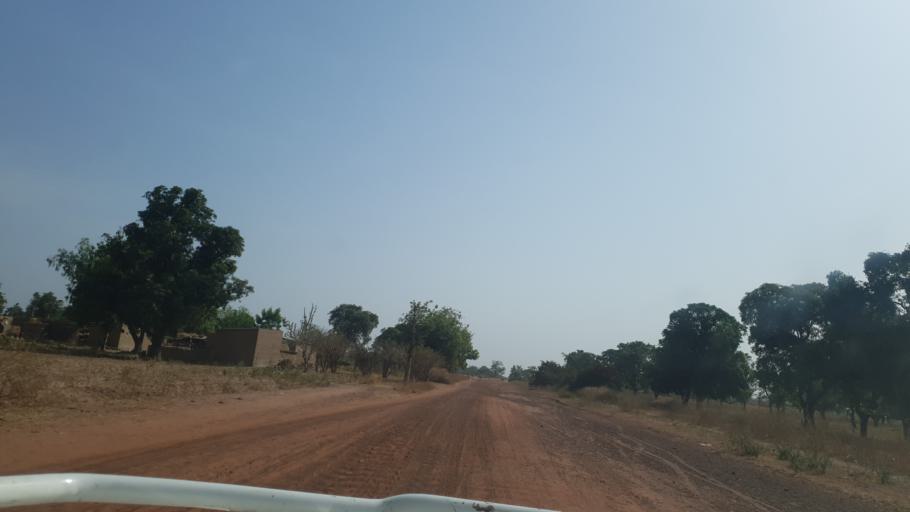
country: ML
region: Koulikoro
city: Dioila
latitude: 12.6690
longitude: -6.6739
